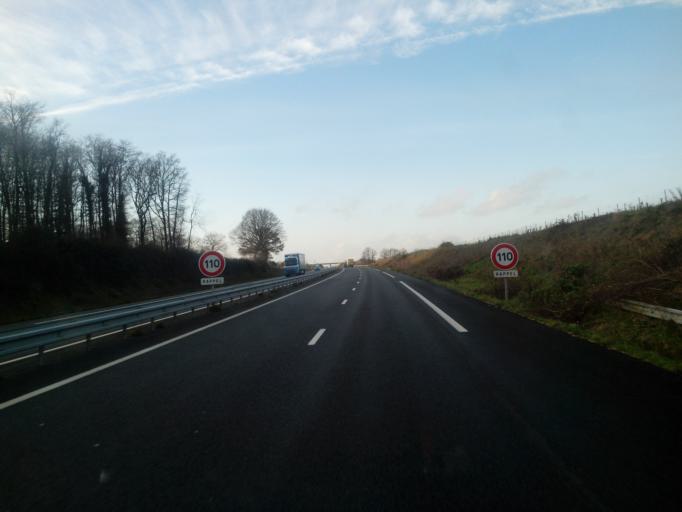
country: FR
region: Poitou-Charentes
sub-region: Departement des Deux-Sevres
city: Combrand
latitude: 46.9237
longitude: -0.7043
